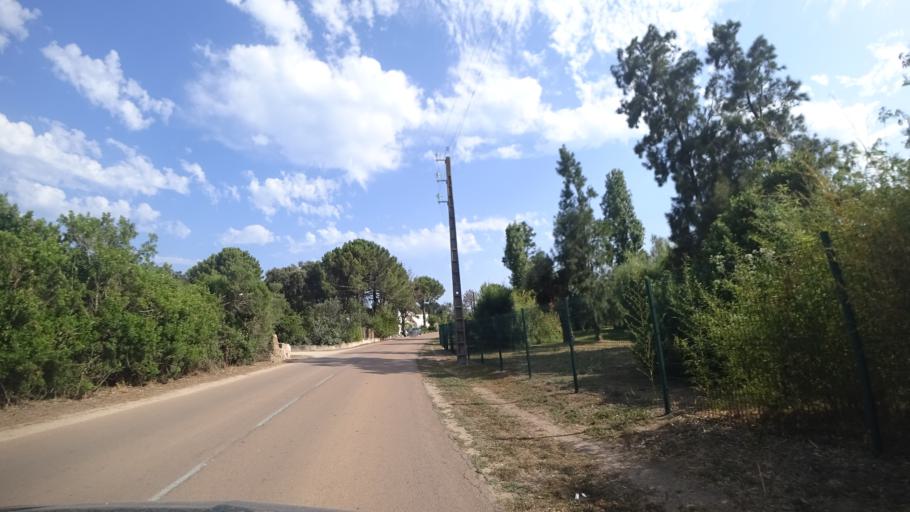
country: FR
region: Corsica
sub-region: Departement de la Corse-du-Sud
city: Porto-Vecchio
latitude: 41.6262
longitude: 9.3366
